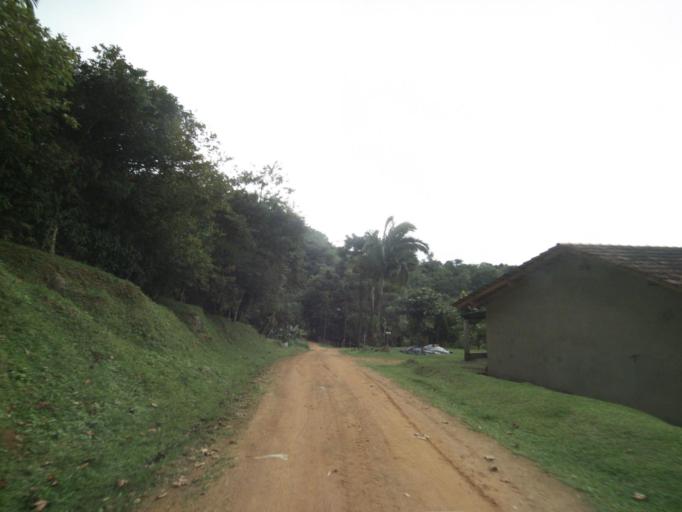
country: BR
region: Santa Catarina
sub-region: Pomerode
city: Pomerode
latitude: -26.7367
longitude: -49.1978
